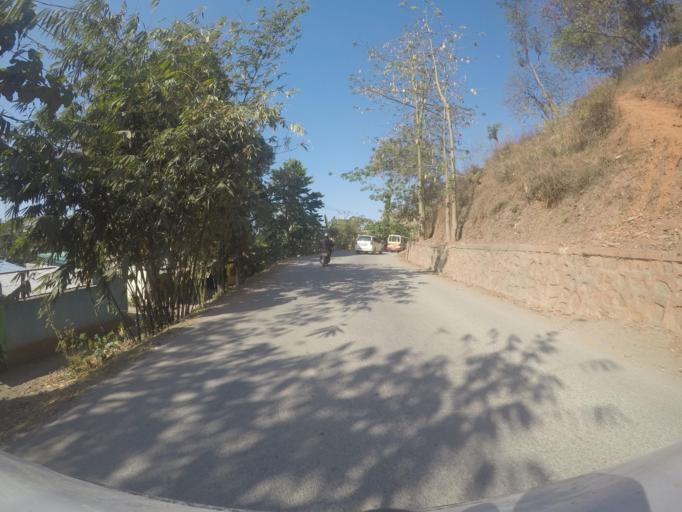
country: TL
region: Dili
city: Dili
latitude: -8.5694
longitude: 125.5442
